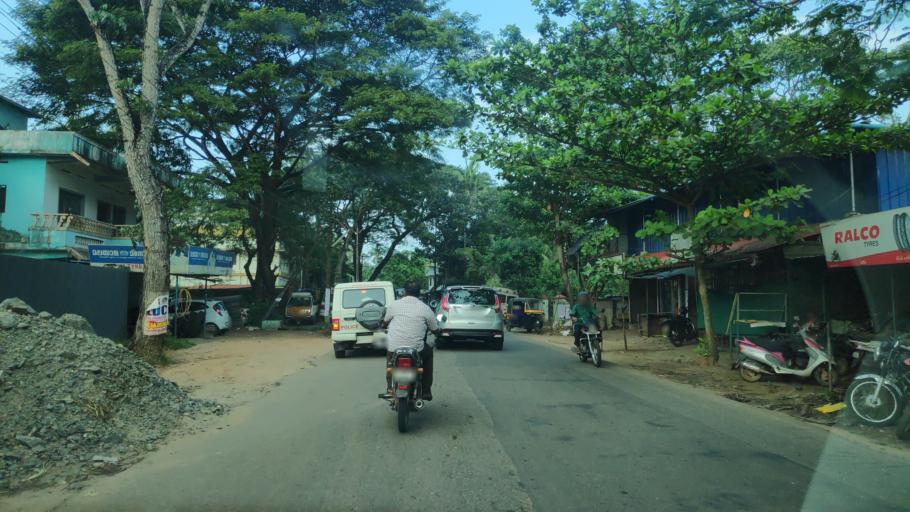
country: IN
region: Kerala
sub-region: Alappuzha
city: Alleppey
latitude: 9.5665
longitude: 76.3475
